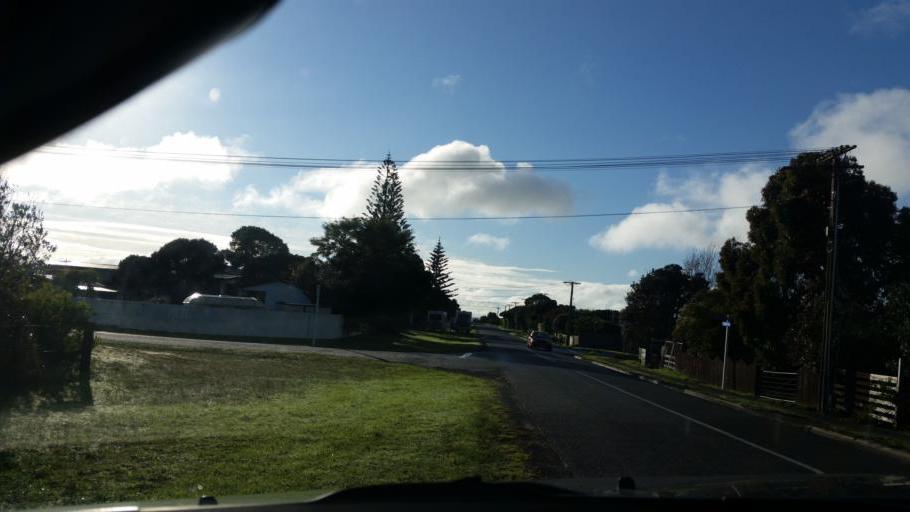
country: NZ
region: Auckland
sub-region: Auckland
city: Wellsford
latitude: -36.0910
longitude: 174.5855
